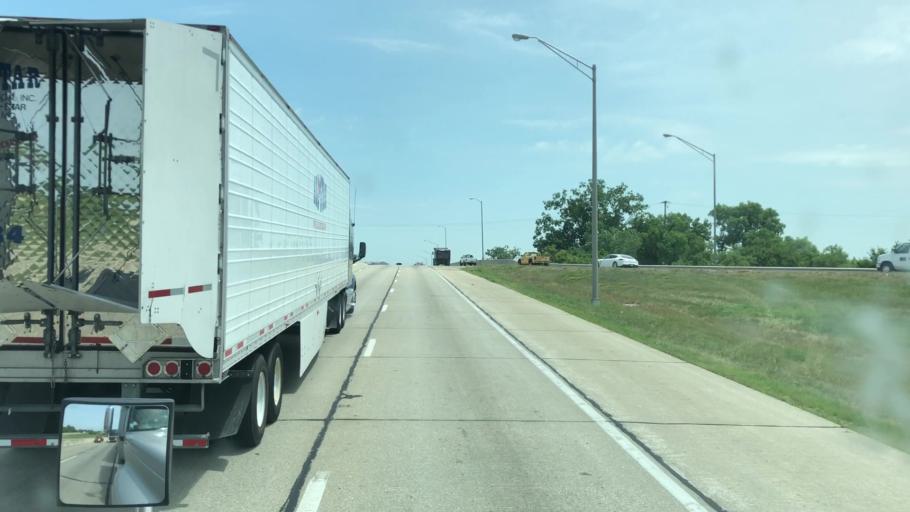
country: US
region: Indiana
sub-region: Marion County
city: Indianapolis
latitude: 39.7521
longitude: -86.2228
